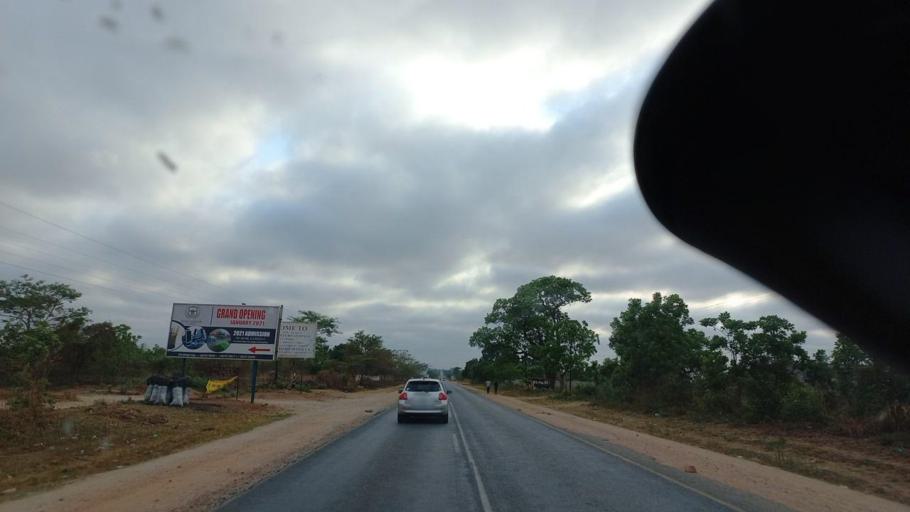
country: ZM
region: Lusaka
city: Lusaka
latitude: -15.3555
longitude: 28.4818
